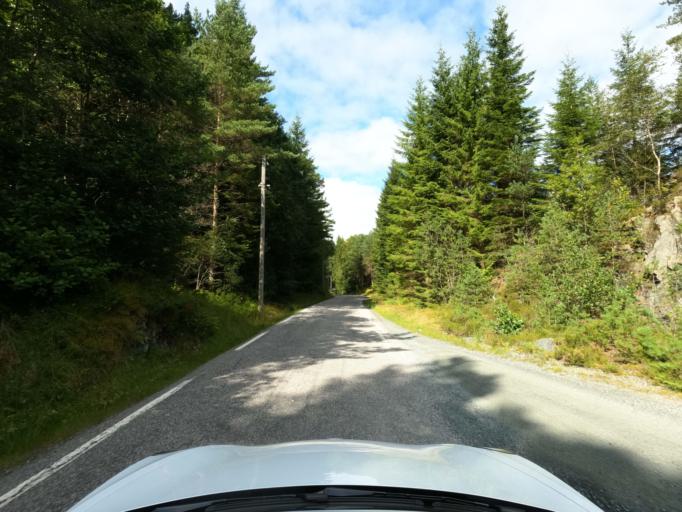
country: NO
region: Hordaland
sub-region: Os
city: Hagavik
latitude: 60.1686
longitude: 5.3653
